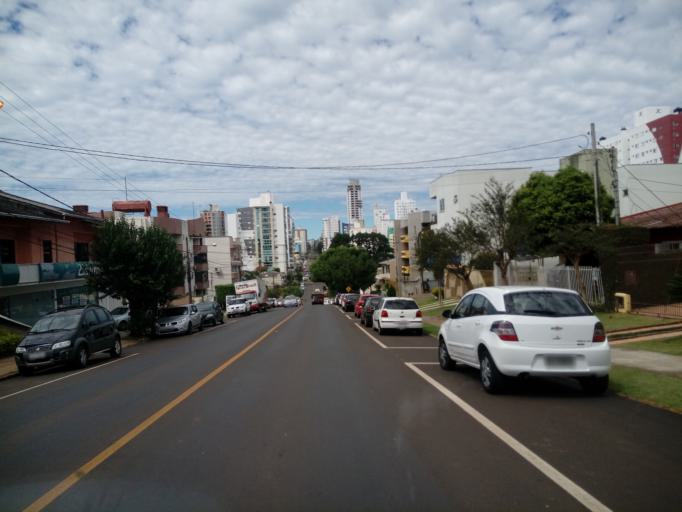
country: BR
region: Santa Catarina
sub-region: Chapeco
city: Chapeco
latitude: -27.0953
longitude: -52.6103
